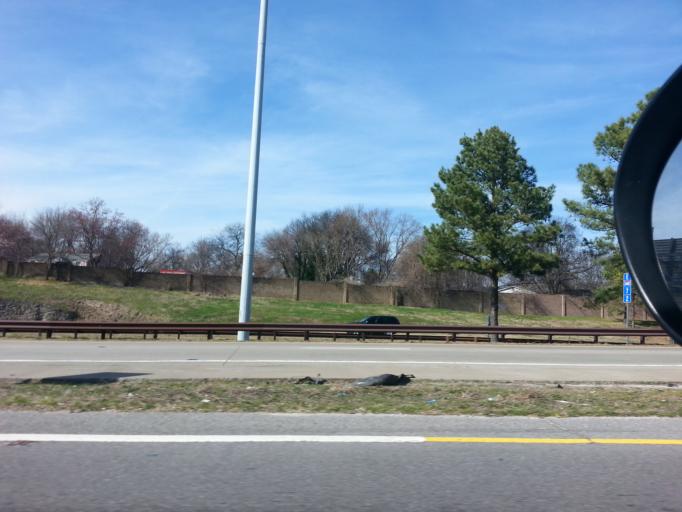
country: US
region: Tennessee
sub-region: Davidson County
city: Oak Hill
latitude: 36.1254
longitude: -86.7321
